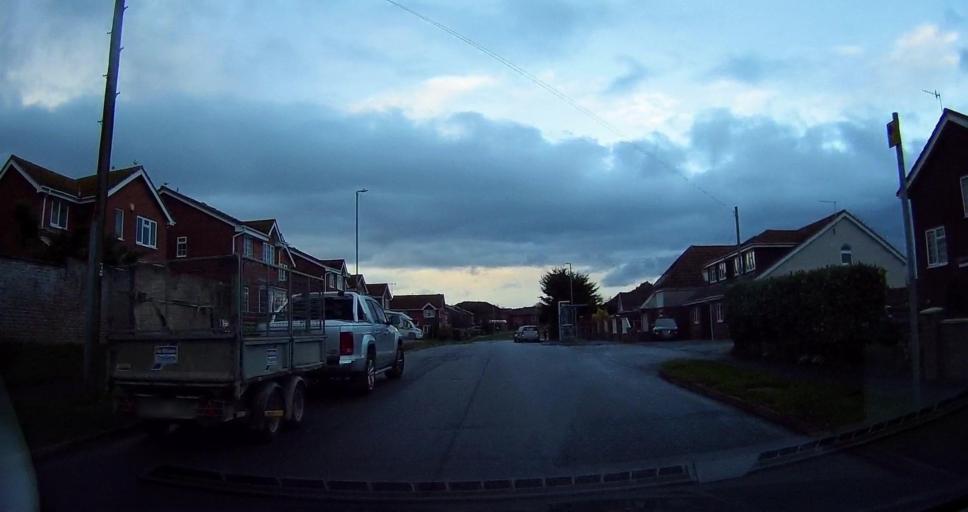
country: GB
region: England
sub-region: East Sussex
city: Peacehaven
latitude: 50.8024
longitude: -0.0052
